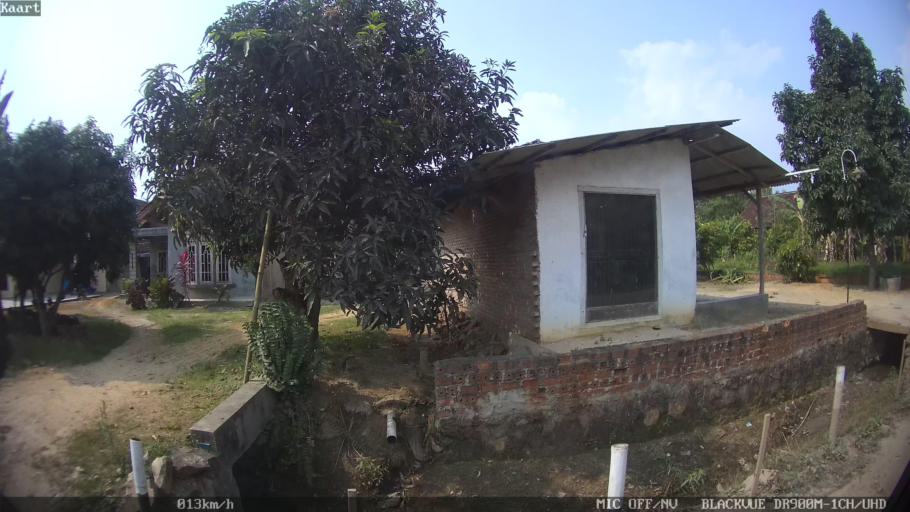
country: ID
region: Lampung
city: Kedondong
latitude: -5.4095
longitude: 105.0047
